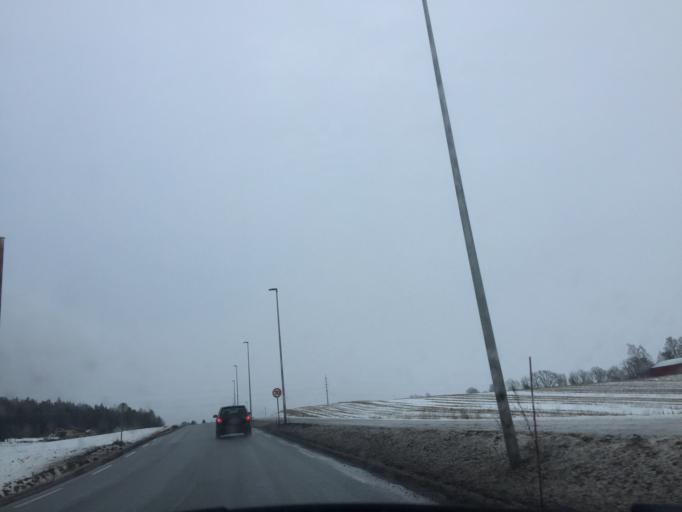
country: NO
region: Akershus
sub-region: Frogn
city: Drobak
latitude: 59.6604
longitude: 10.6688
